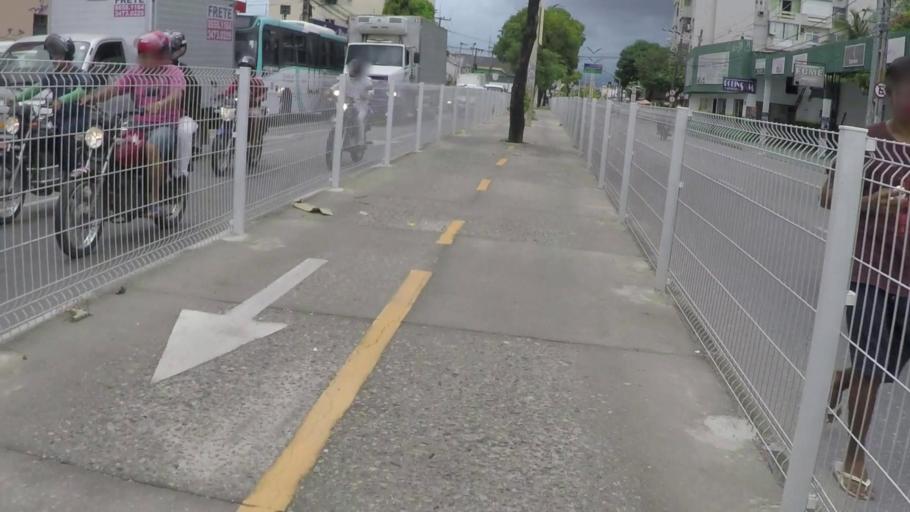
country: BR
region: Ceara
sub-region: Fortaleza
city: Fortaleza
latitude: -3.7357
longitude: -38.5340
